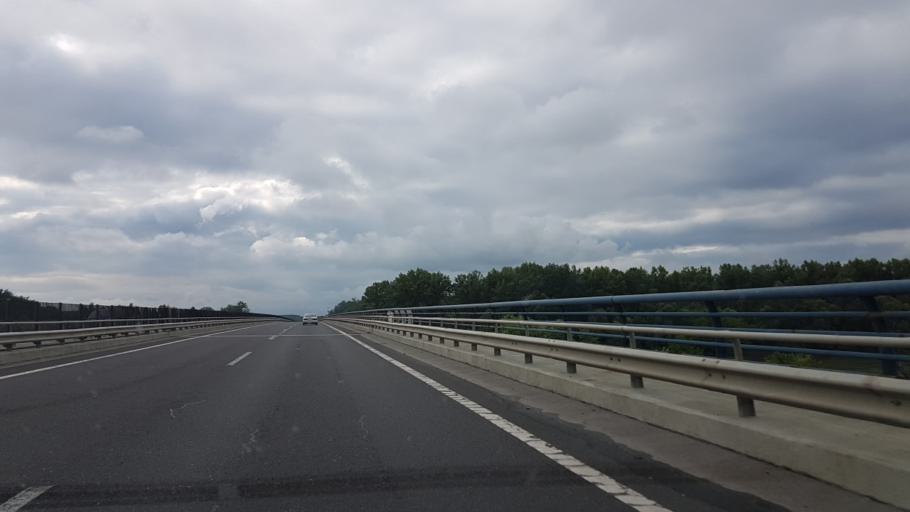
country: HU
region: Hajdu-Bihar
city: Polgar
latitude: 47.8548
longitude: 21.0559
